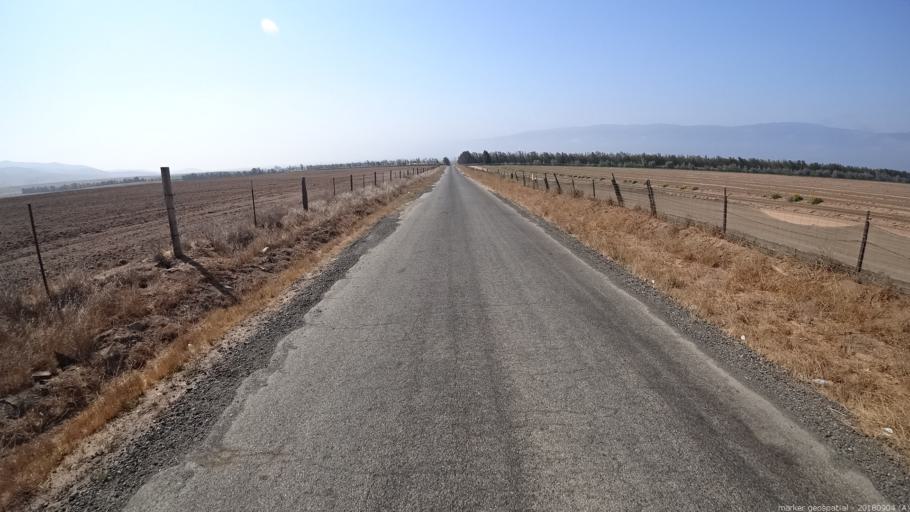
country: US
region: California
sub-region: Monterey County
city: Gonzales
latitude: 36.5007
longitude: -121.3648
